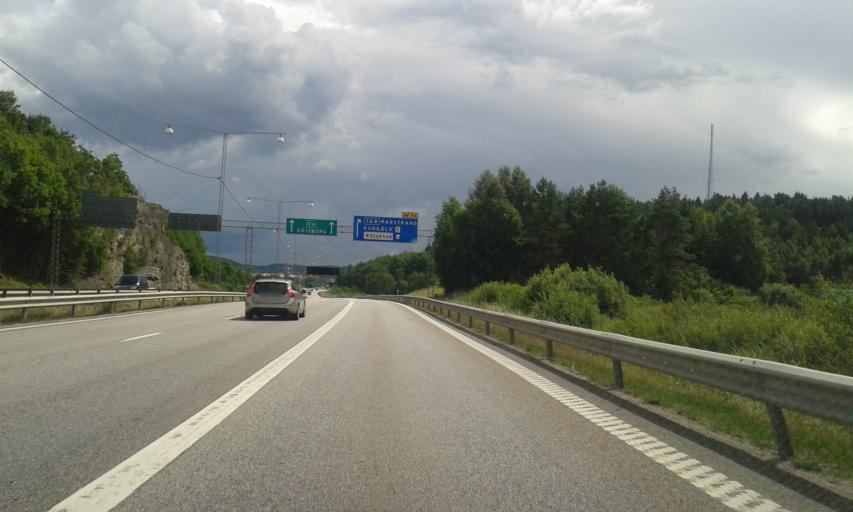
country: SE
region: Vaestra Goetaland
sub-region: Kungalvs Kommun
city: Kungalv
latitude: 57.8817
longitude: 11.9499
